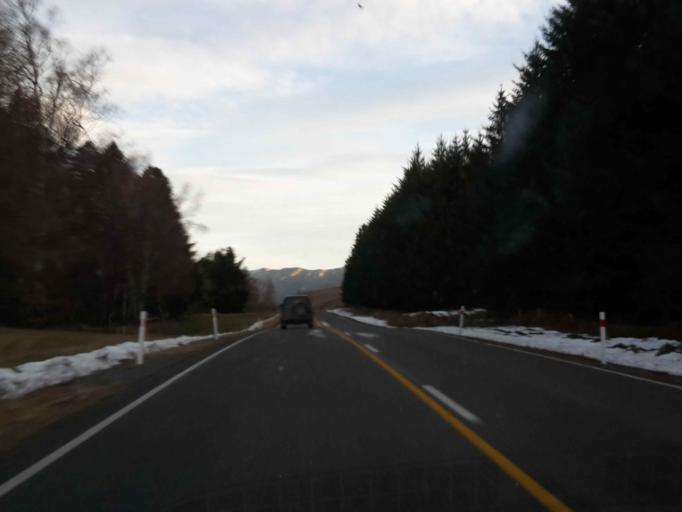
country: NZ
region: Canterbury
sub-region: Timaru District
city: Pleasant Point
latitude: -44.0470
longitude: 170.6824
